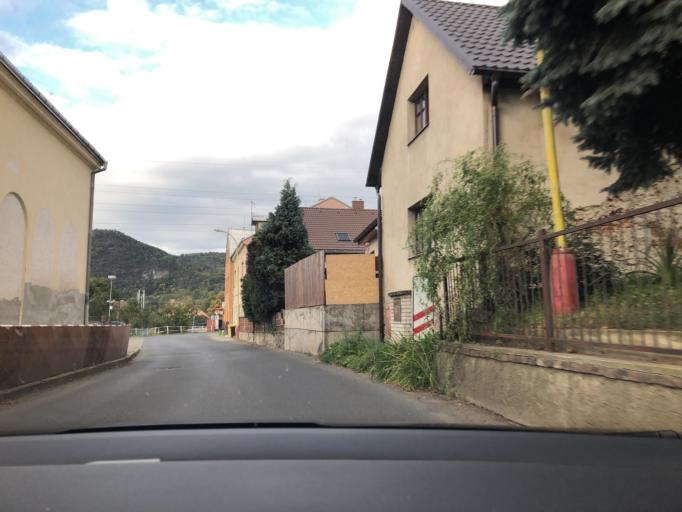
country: CZ
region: Ustecky
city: Velke Brezno
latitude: 50.6620
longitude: 14.1414
